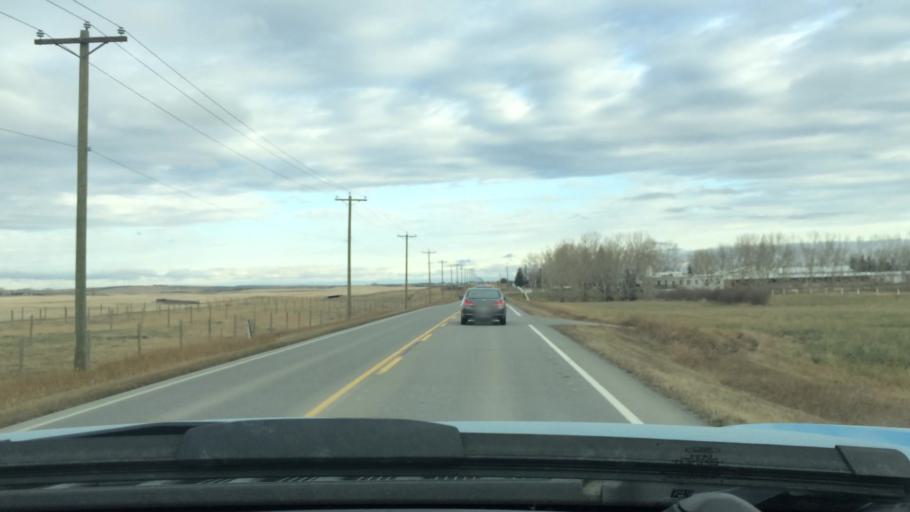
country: CA
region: Alberta
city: Airdrie
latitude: 51.2286
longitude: -114.0250
